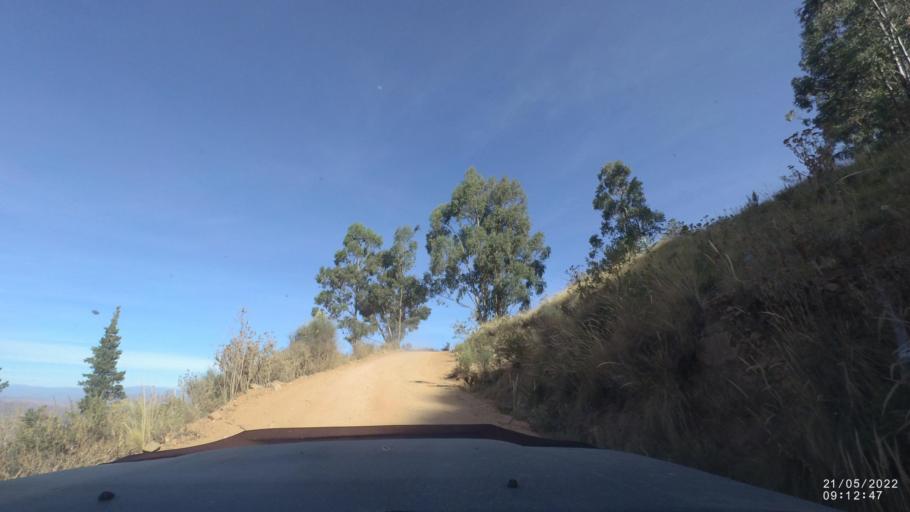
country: BO
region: Cochabamba
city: Cochabamba
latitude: -17.3672
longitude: -66.0234
